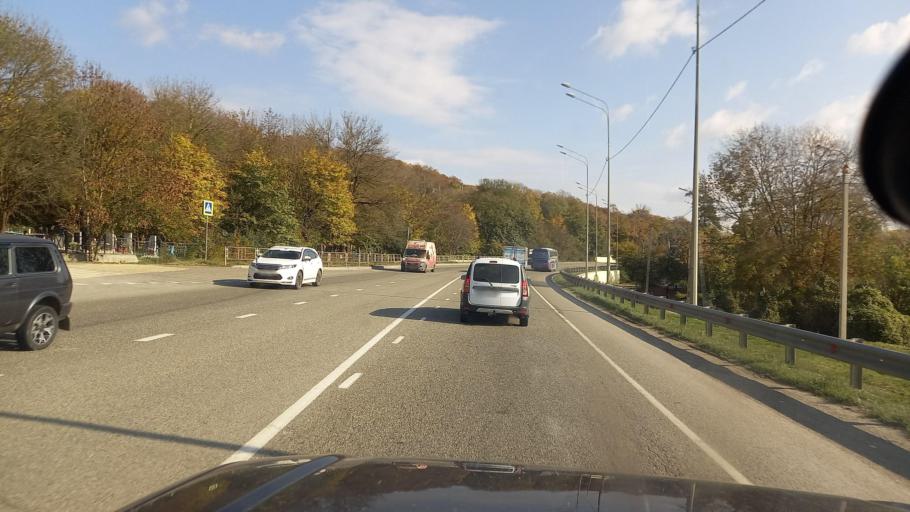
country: RU
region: Krasnodarskiy
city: Verkhnebakanskiy
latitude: 44.8686
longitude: 37.7472
